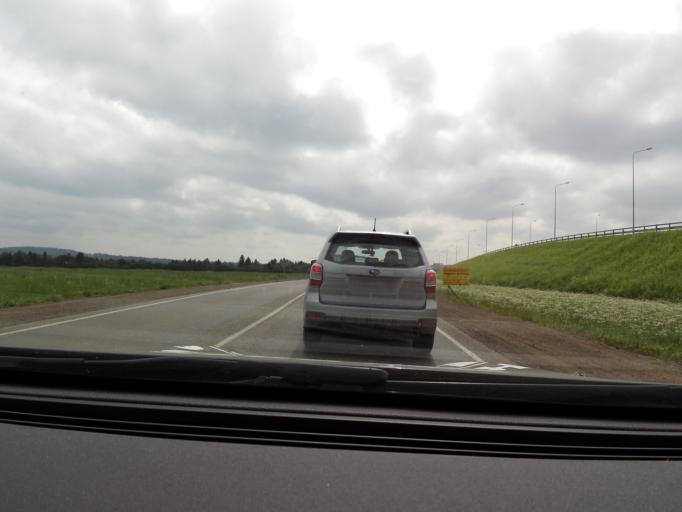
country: RU
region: Perm
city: Zvezdnyy
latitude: 57.7832
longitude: 56.3432
